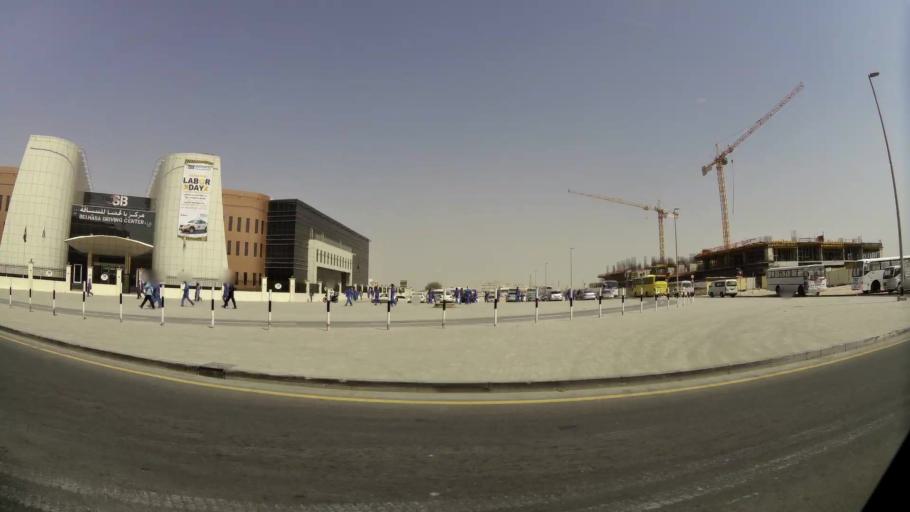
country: AE
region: Dubai
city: Dubai
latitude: 25.1555
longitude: 55.2483
